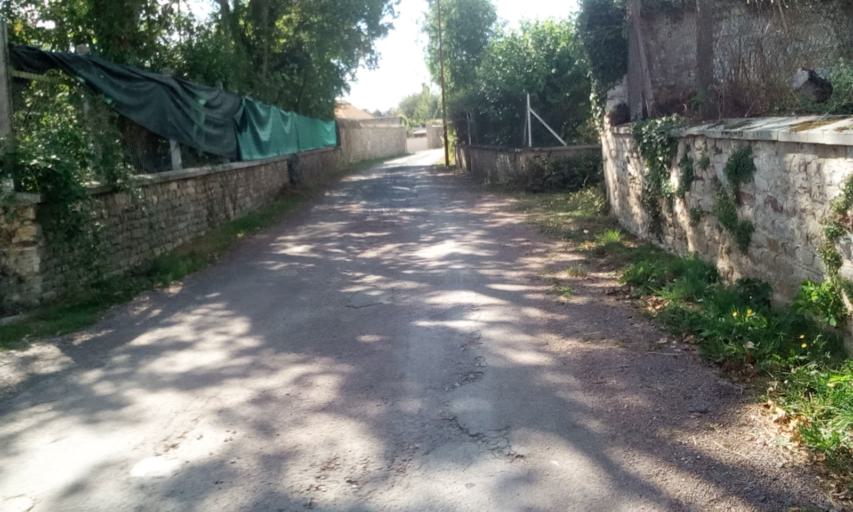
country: FR
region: Lower Normandy
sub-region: Departement du Calvados
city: Bully
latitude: 49.1107
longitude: -0.4343
